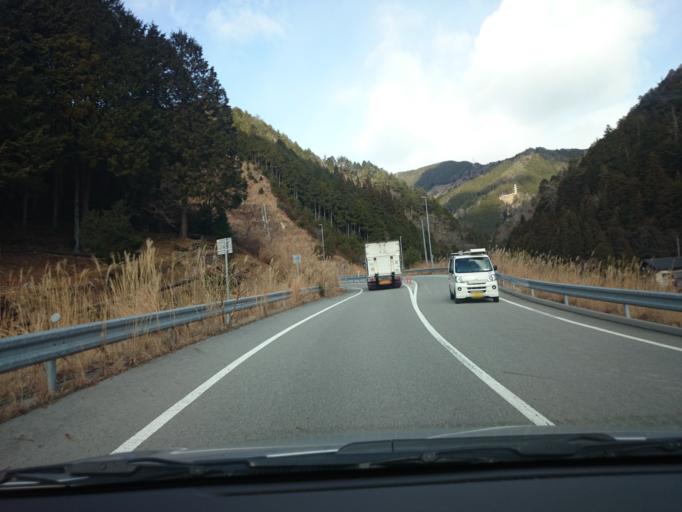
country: JP
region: Gifu
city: Gujo
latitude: 35.7483
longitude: 137.2077
